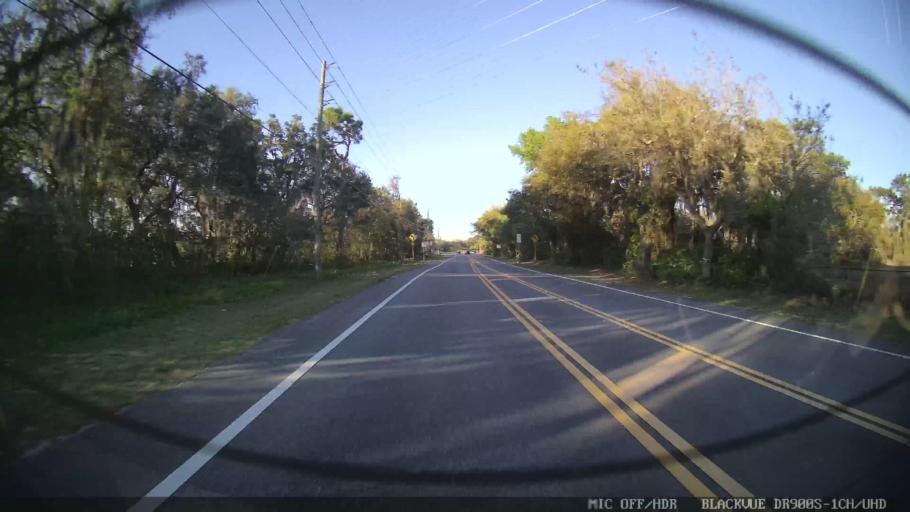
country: US
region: Florida
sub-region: Pasco County
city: Shady Hills
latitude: 28.3420
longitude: -82.5439
